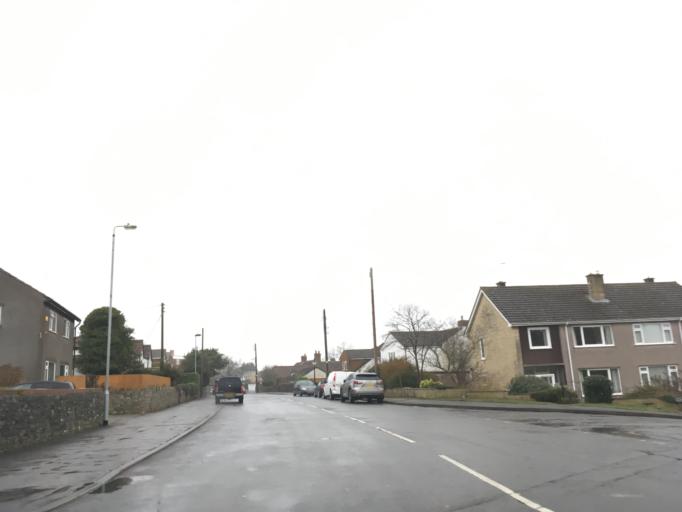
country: GB
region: England
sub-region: South Gloucestershire
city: Alveston
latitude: 51.5895
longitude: -2.5344
